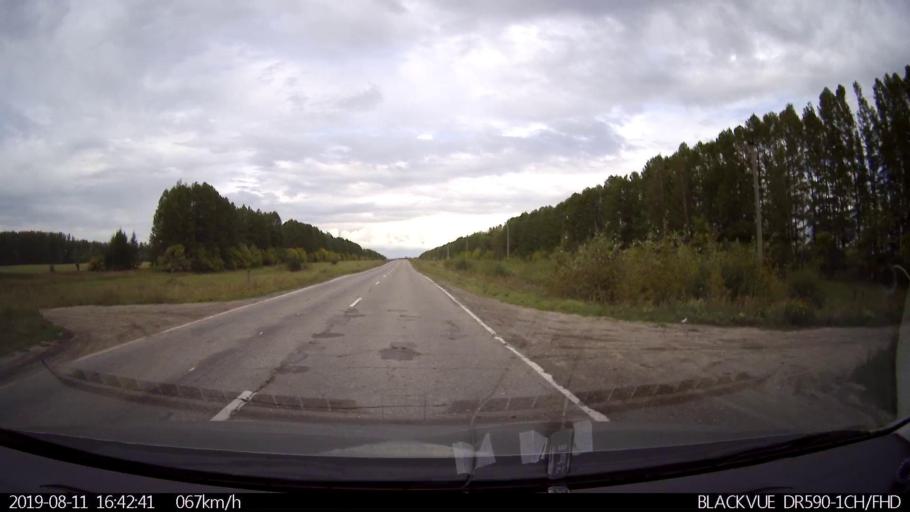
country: RU
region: Ulyanovsk
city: Mayna
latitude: 54.1624
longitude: 47.6646
